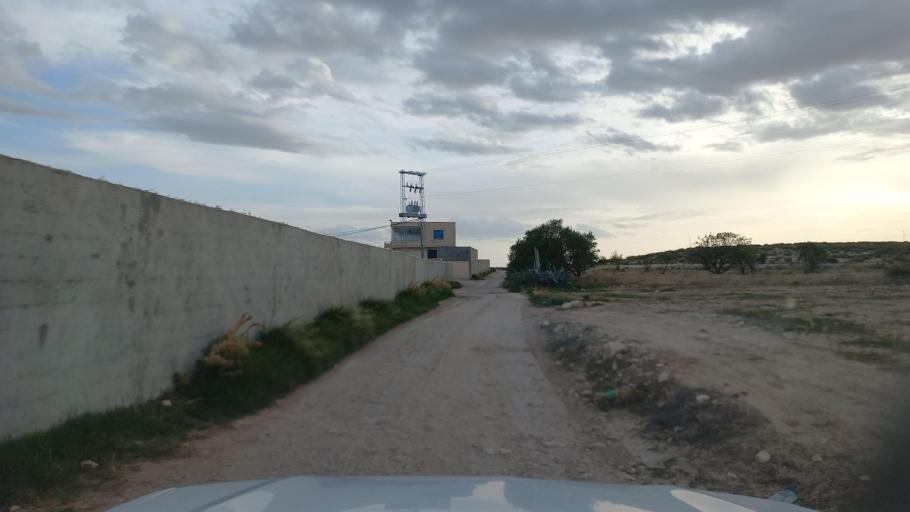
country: TN
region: Al Qasrayn
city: Sbiba
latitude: 35.4267
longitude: 9.0964
